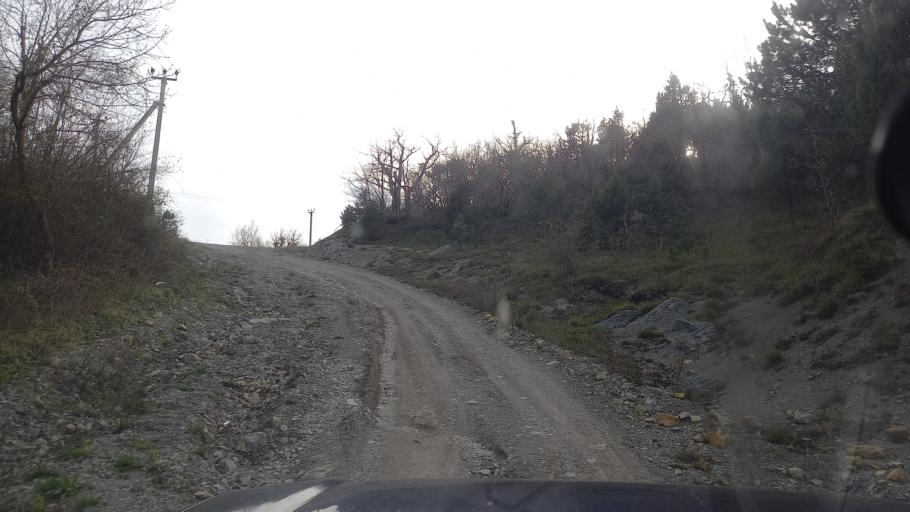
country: RU
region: Krasnodarskiy
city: Arkhipo-Osipovka
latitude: 44.3668
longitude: 38.5824
